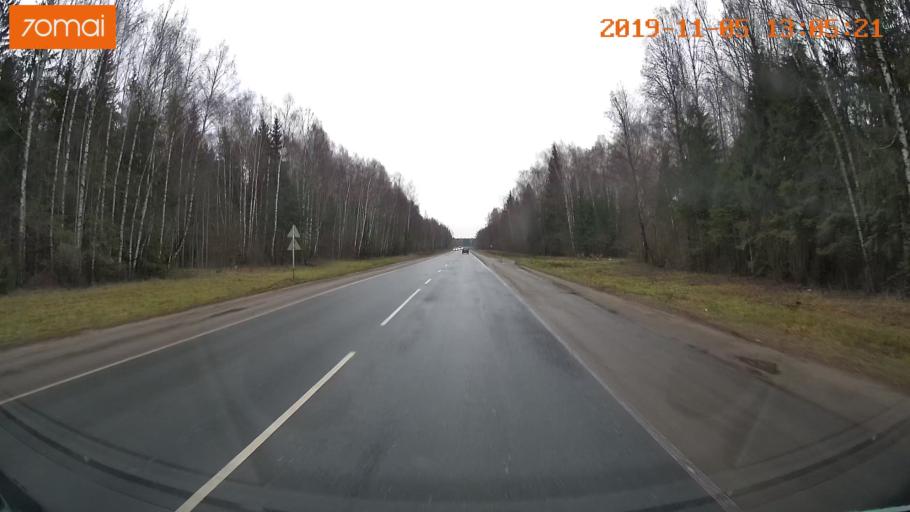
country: RU
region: Ivanovo
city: Kitovo
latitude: 56.8831
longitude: 41.2407
